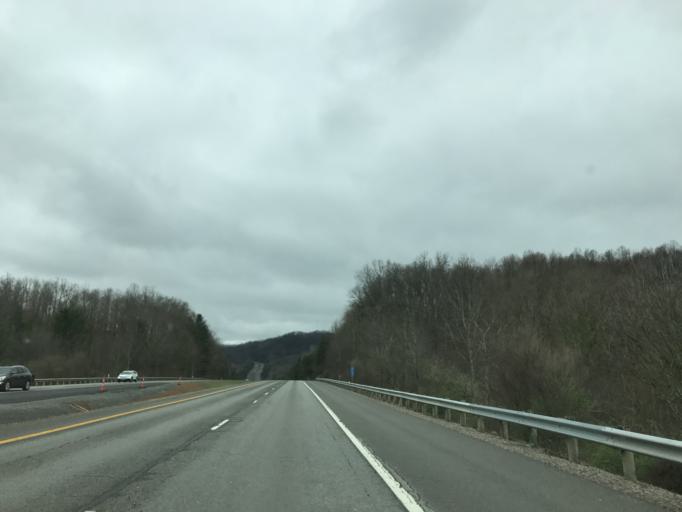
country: US
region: West Virginia
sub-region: Fayette County
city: Mount Hope
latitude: 37.9053
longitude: -81.1731
